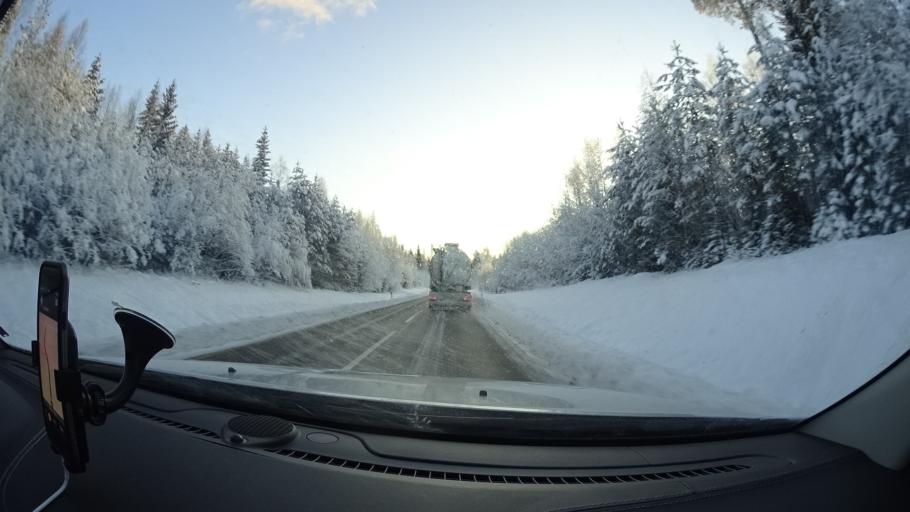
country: SE
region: Jaemtland
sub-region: Ragunda Kommun
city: Hammarstrand
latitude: 62.9508
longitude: 16.6926
